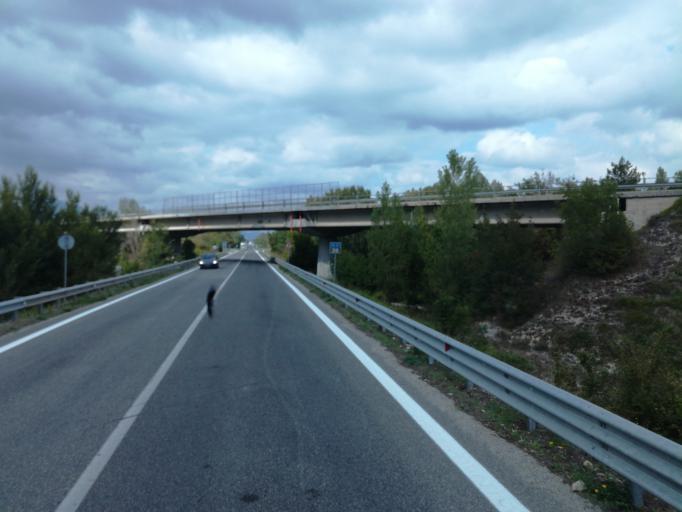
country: IT
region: Molise
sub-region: Provincia di Campobasso
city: Bojano
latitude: 41.4852
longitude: 14.4899
